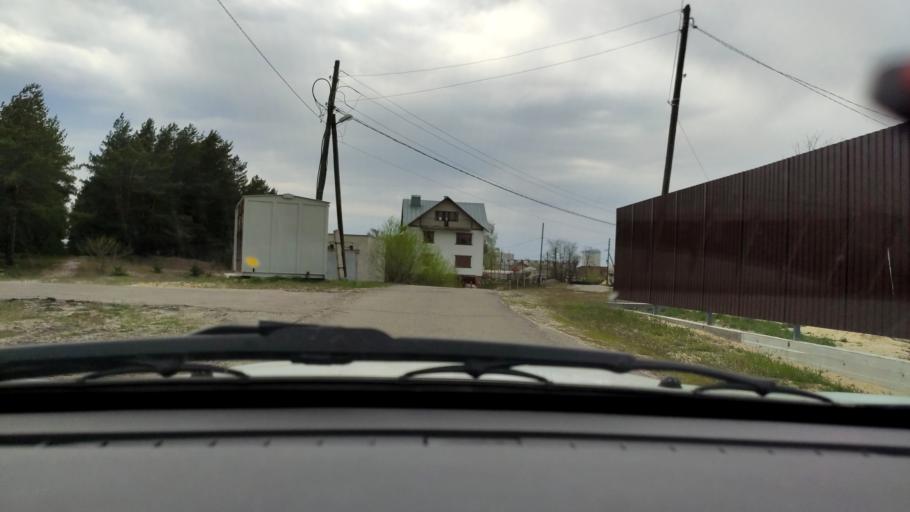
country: RU
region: Voronezj
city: Somovo
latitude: 51.7341
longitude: 39.3364
